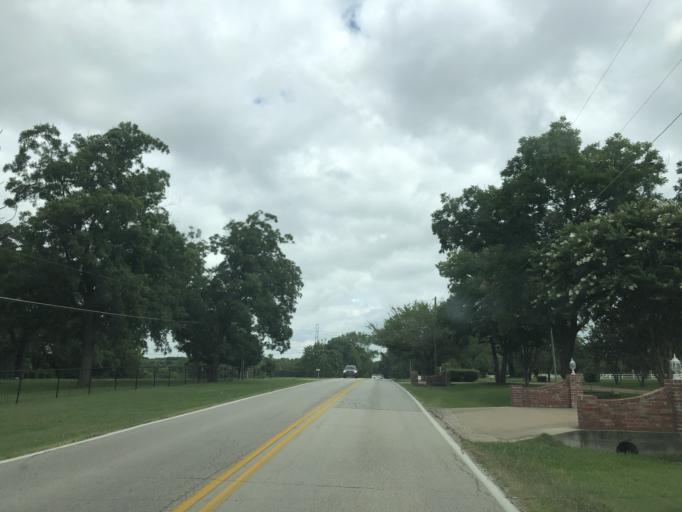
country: US
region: Texas
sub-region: Dallas County
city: Sunnyvale
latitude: 32.8299
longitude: -96.5599
